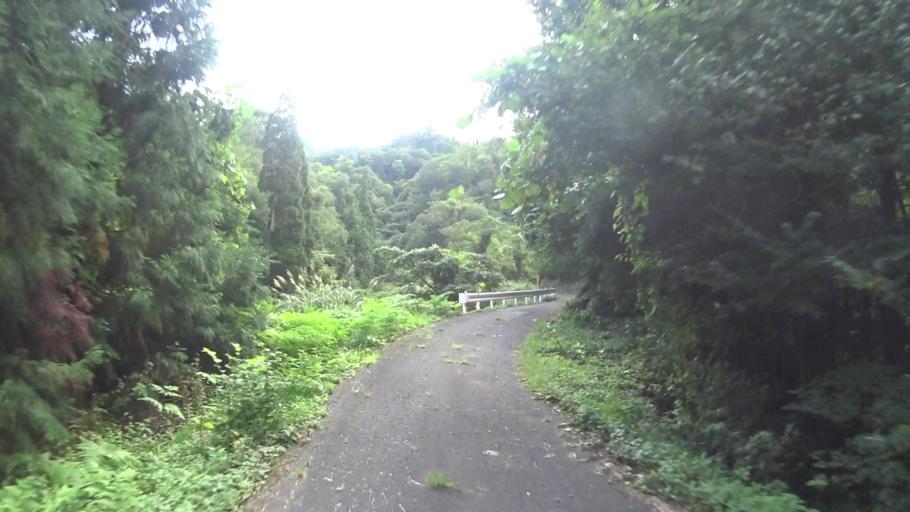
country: JP
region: Kyoto
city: Miyazu
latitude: 35.6688
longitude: 135.1399
